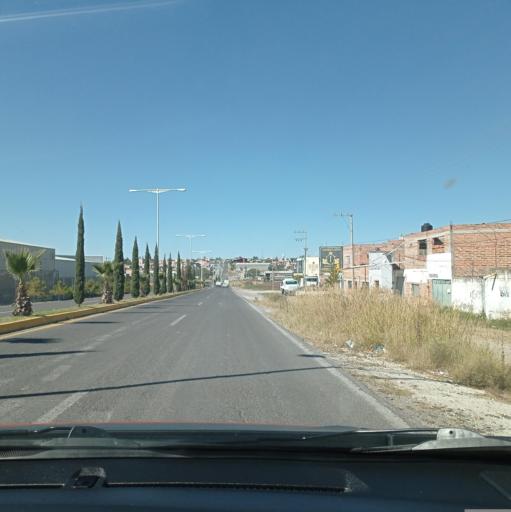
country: MX
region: Jalisco
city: San Miguel el Alto
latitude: 21.0328
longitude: -102.3949
